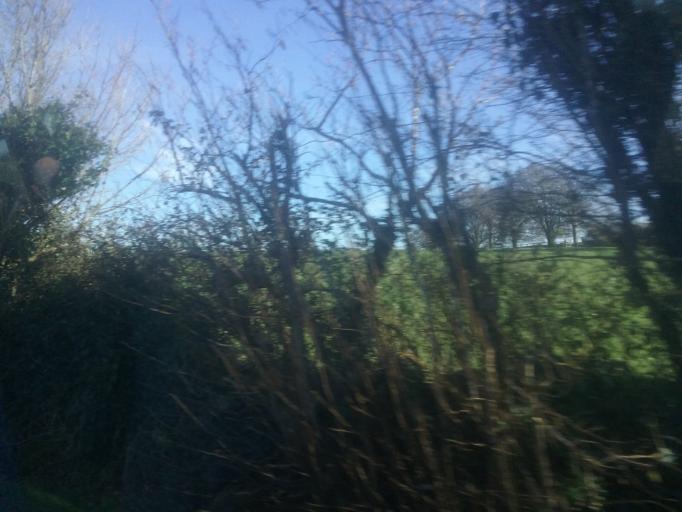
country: IE
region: Munster
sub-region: An Clar
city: Ennis
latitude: 52.9985
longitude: -8.9643
